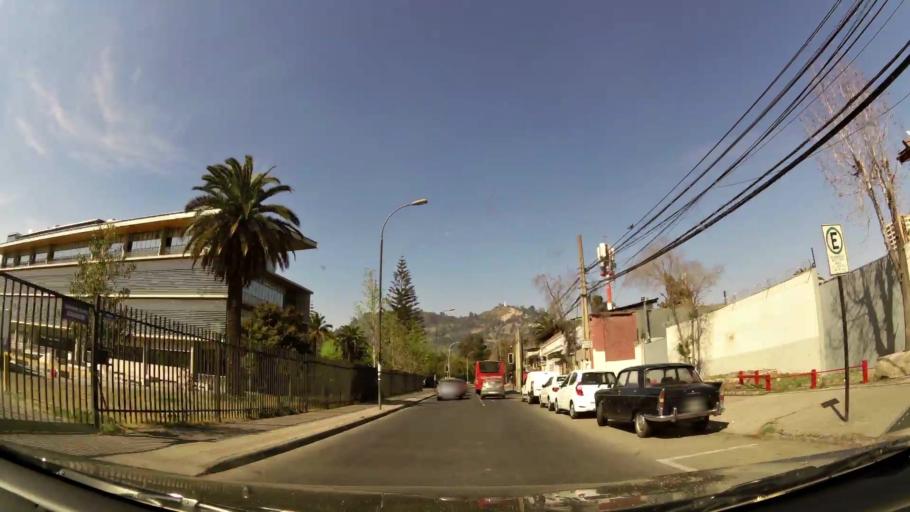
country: CL
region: Santiago Metropolitan
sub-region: Provincia de Santiago
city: Santiago
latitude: -33.4233
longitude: -70.6517
